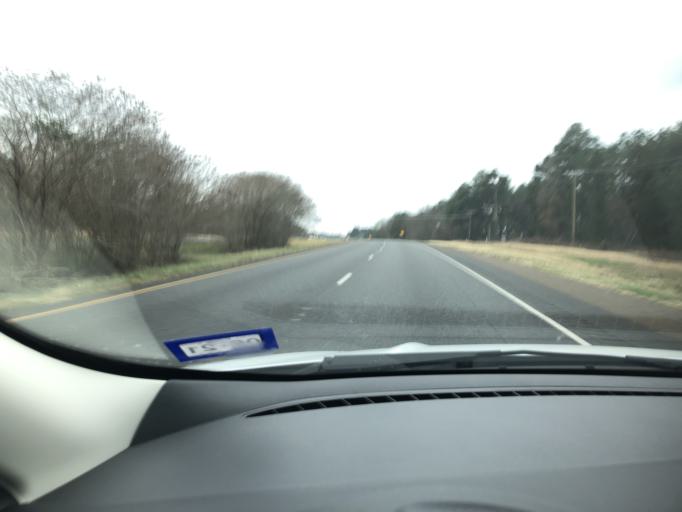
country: US
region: Texas
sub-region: Nacogdoches County
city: Nacogdoches
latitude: 31.5372
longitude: -94.6932
